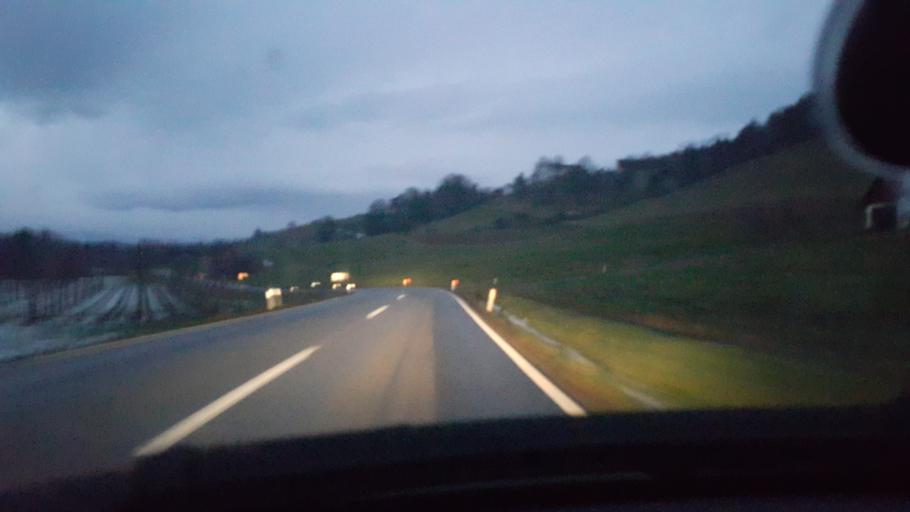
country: AT
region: Styria
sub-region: Politischer Bezirk Leibnitz
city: Arnfels
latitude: 46.6713
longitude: 15.4321
